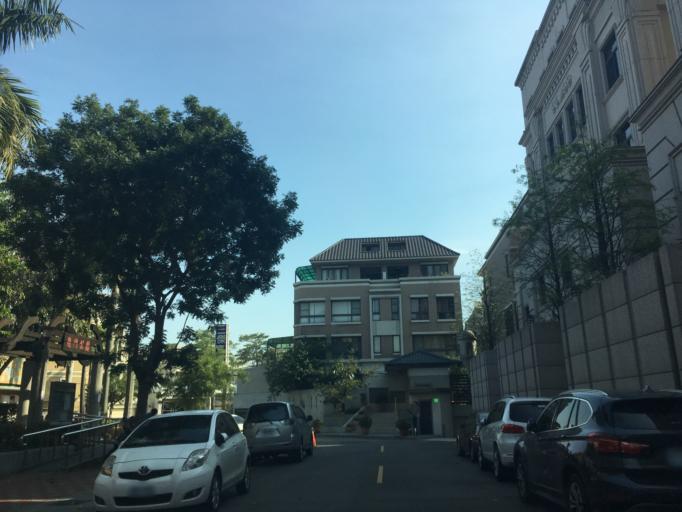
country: TW
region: Taiwan
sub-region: Taichung City
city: Taichung
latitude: 24.1646
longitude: 120.6315
